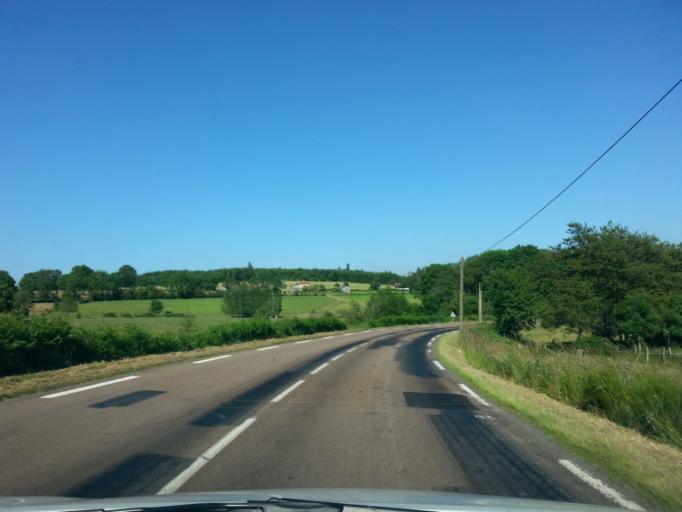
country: FR
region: Rhone-Alpes
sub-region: Departement du Rhone
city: Beaujeu
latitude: 46.1707
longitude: 4.4823
